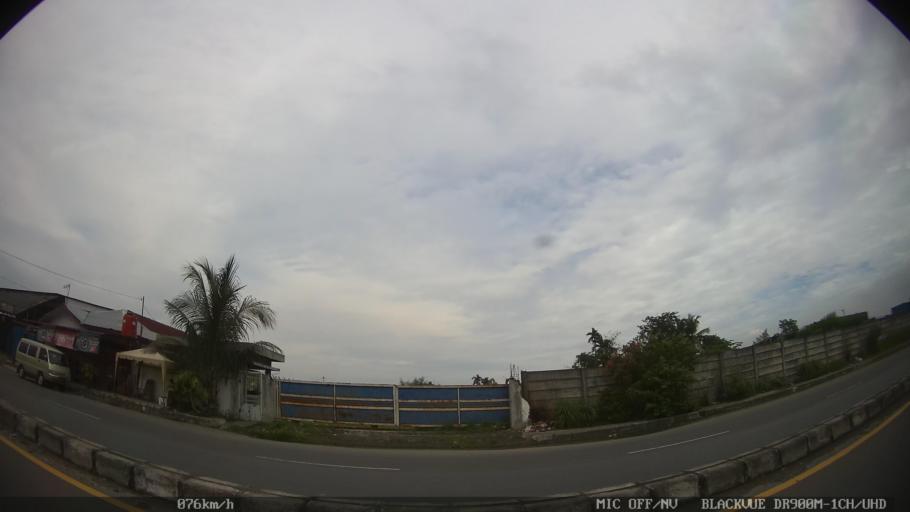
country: ID
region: North Sumatra
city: Sunggal
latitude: 3.6140
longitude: 98.5759
